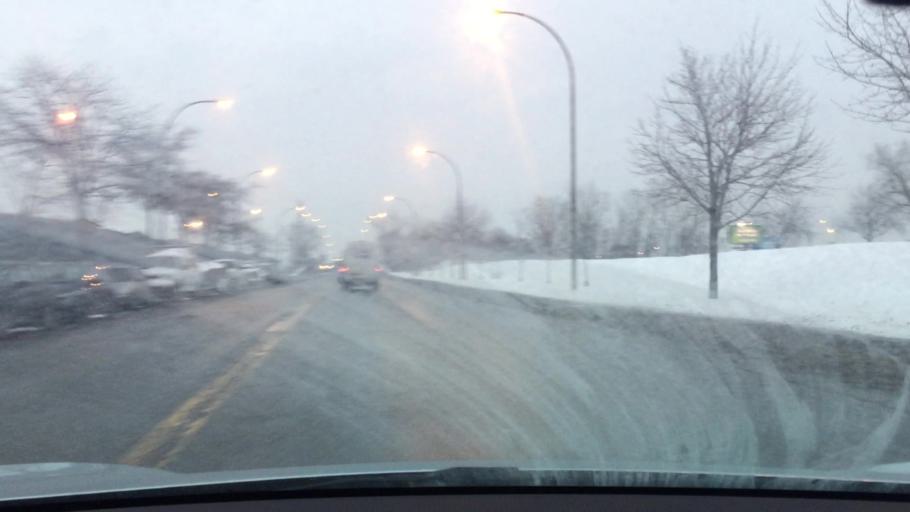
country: CA
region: Quebec
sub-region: Monteregie
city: Longueuil
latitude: 45.5309
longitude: -73.5448
